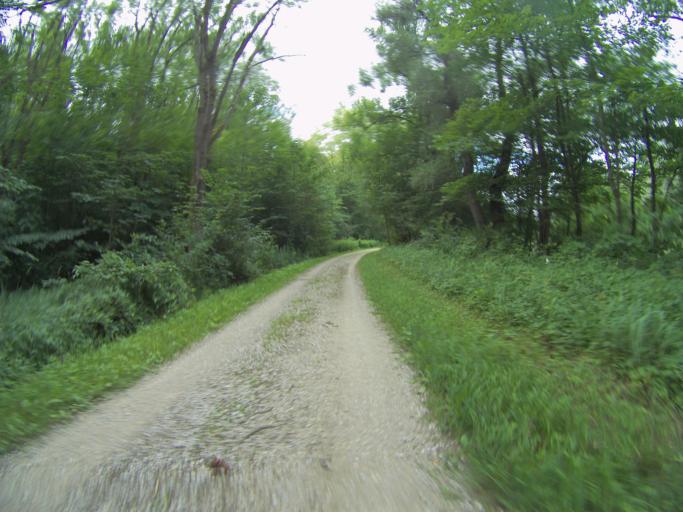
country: DE
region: Bavaria
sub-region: Upper Bavaria
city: Hallbergmoos
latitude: 48.3541
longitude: 11.7264
